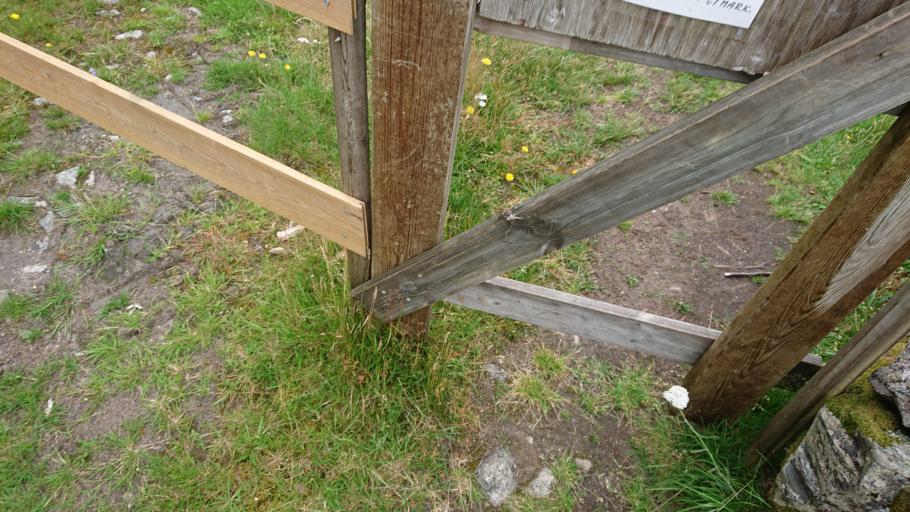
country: NO
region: Rogaland
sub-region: Hjelmeland
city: Hjelmelandsvagen
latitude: 59.1955
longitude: 6.4246
